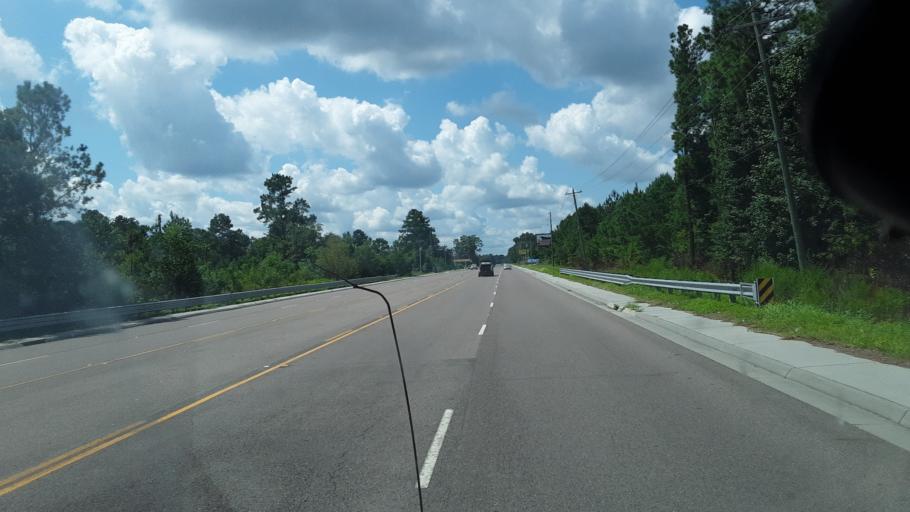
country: US
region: South Carolina
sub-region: Berkeley County
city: Moncks Corner
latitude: 33.1703
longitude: -80.0423
